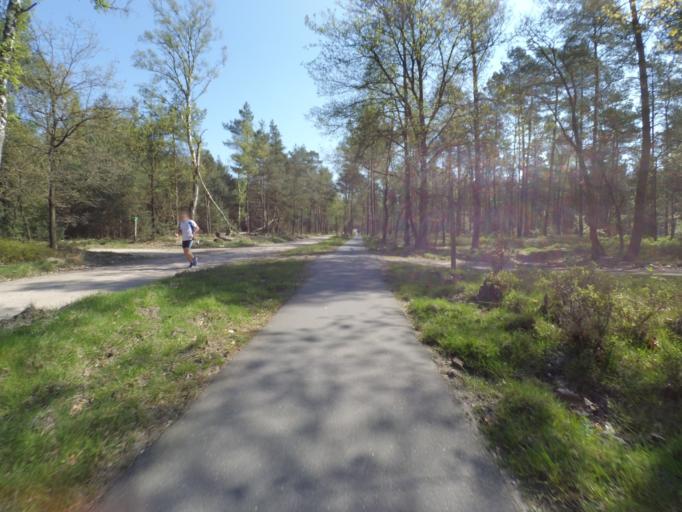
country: NL
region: Gelderland
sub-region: Gemeente Apeldoorn
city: Apeldoorn
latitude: 52.2017
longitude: 5.8932
